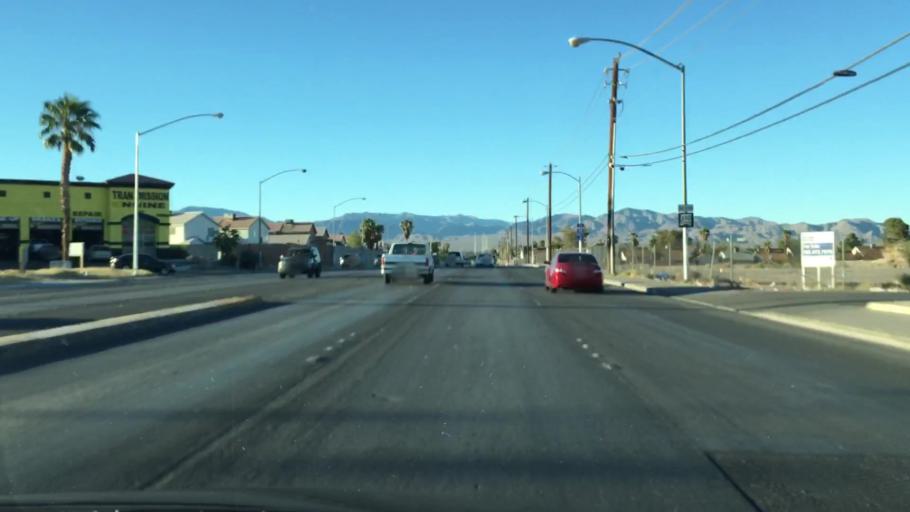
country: US
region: Nevada
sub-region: Clark County
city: Sunrise Manor
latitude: 36.2265
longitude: -115.0801
